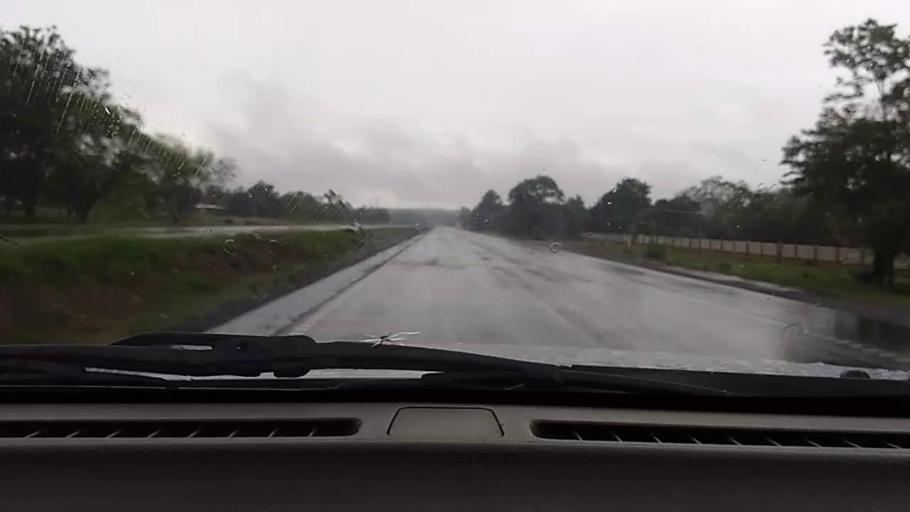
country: PY
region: Caaguazu
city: Repatriacion
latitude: -25.4623
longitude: -55.9270
